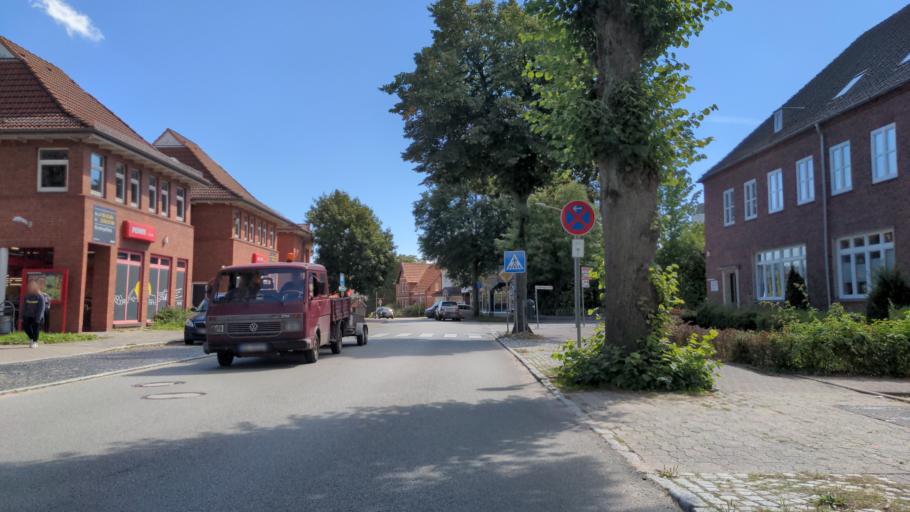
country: DE
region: Schleswig-Holstein
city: Lensahn
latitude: 54.2194
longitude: 10.8883
